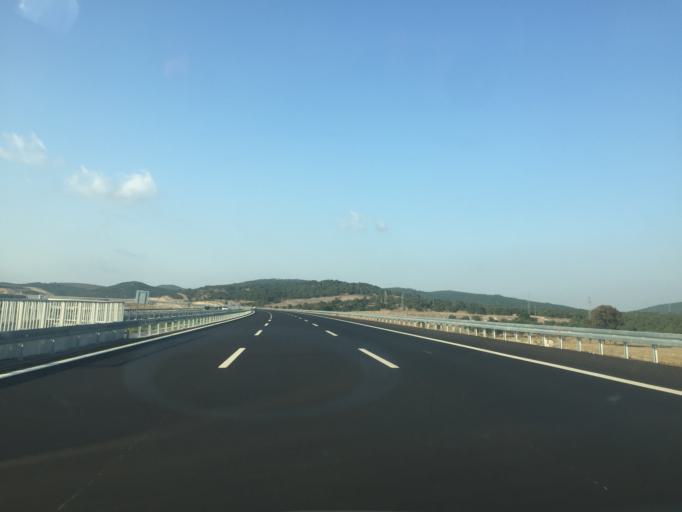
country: TR
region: Balikesir
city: Ertugrul
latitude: 39.5037
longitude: 27.6780
